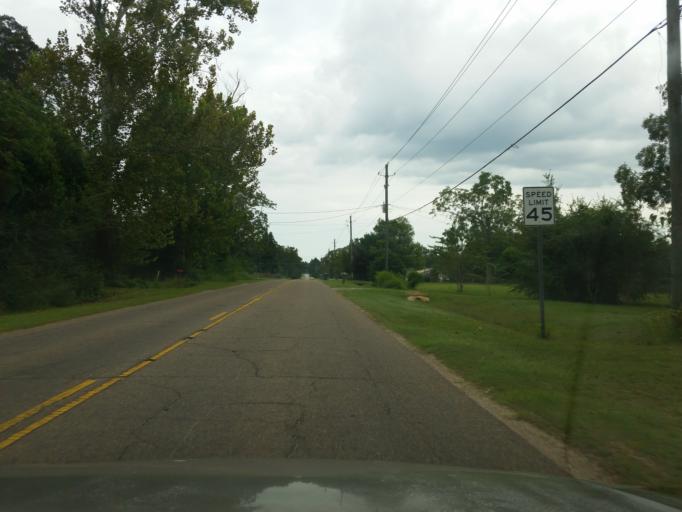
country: US
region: Florida
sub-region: Escambia County
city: Molino
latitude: 30.7238
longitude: -87.3414
